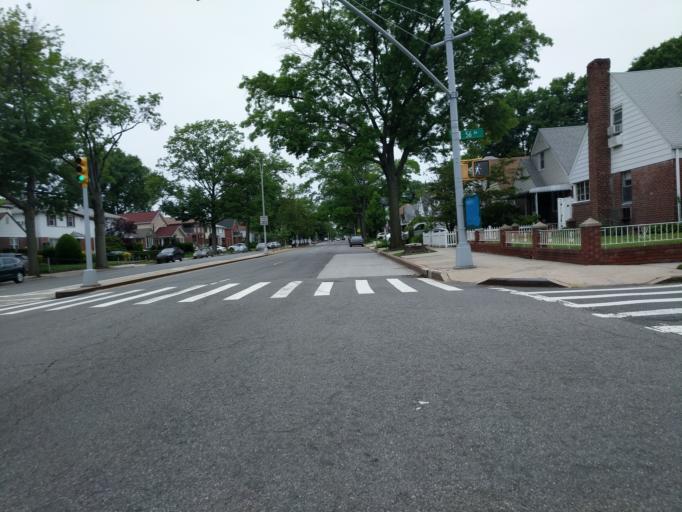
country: US
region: New York
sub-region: Nassau County
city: East Atlantic Beach
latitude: 40.7471
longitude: -73.7775
